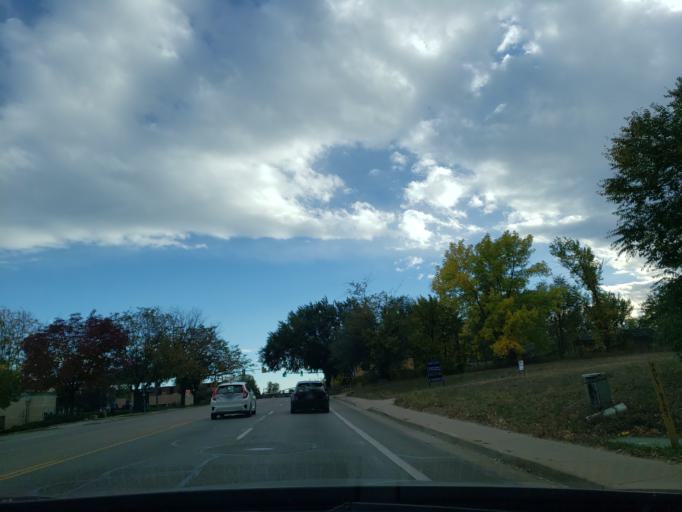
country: US
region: Colorado
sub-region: Larimer County
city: Fort Collins
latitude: 40.5754
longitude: -105.0580
